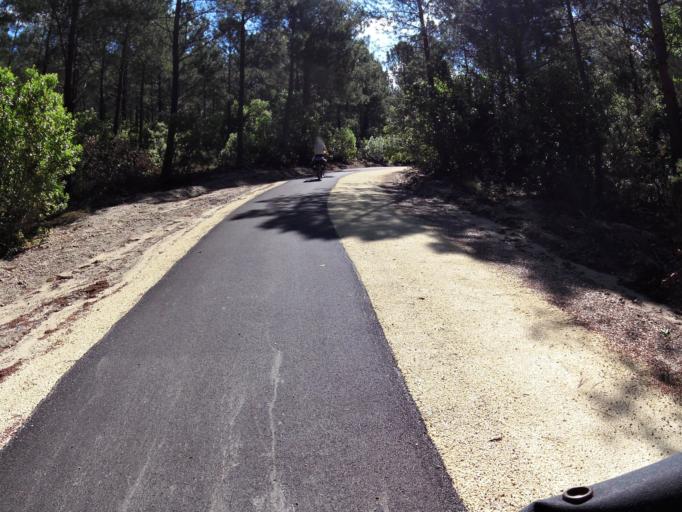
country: FR
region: Aquitaine
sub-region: Departement de la Gironde
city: Lacanau
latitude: 45.0317
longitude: -1.1627
